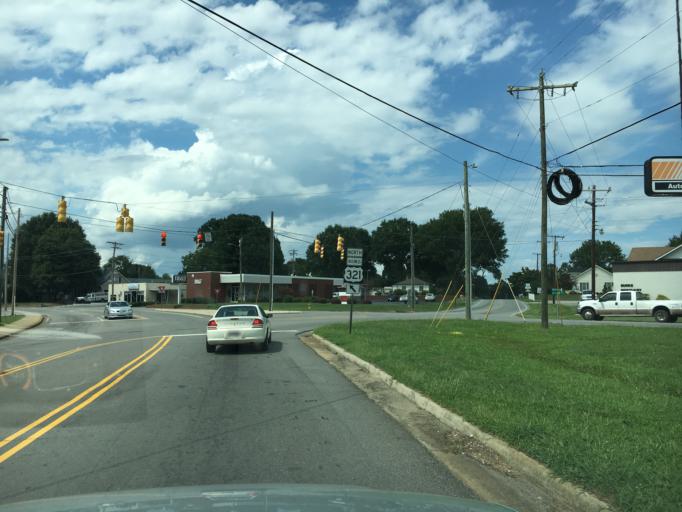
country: US
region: North Carolina
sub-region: Catawba County
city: Maiden
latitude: 35.5695
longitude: -81.1954
